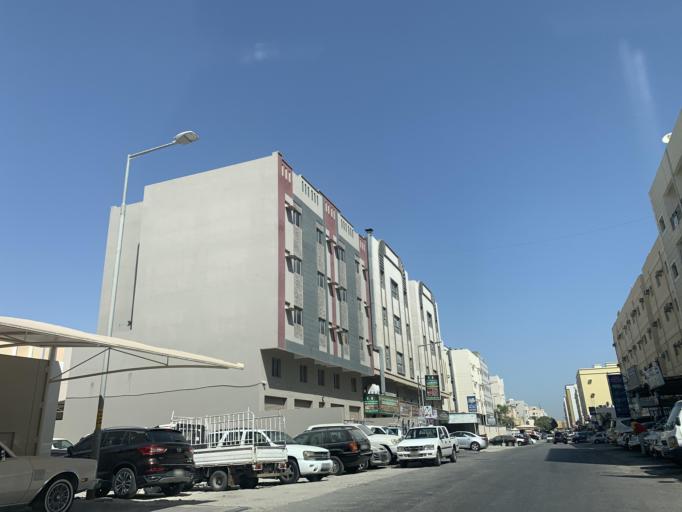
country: BH
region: Northern
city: Ar Rifa'
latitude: 26.1337
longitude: 50.5820
